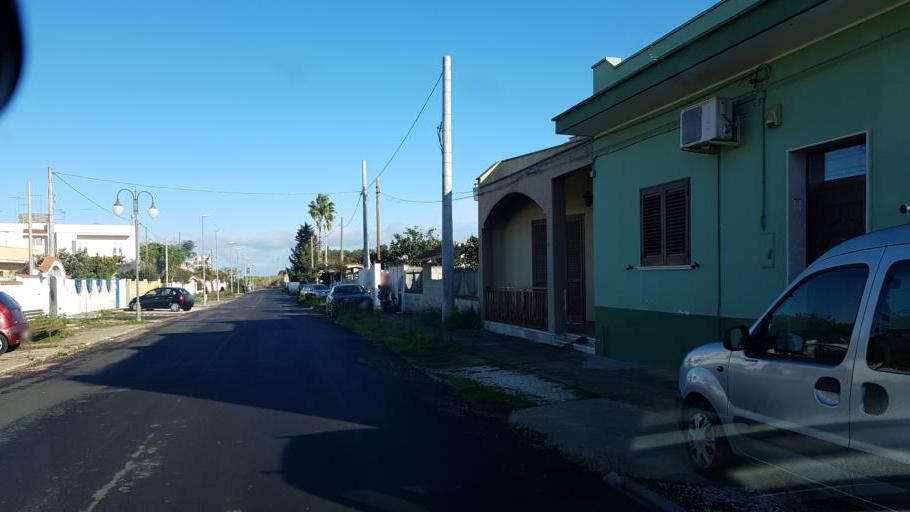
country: IT
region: Apulia
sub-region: Provincia di Brindisi
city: Tuturano
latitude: 40.5469
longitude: 17.9472
